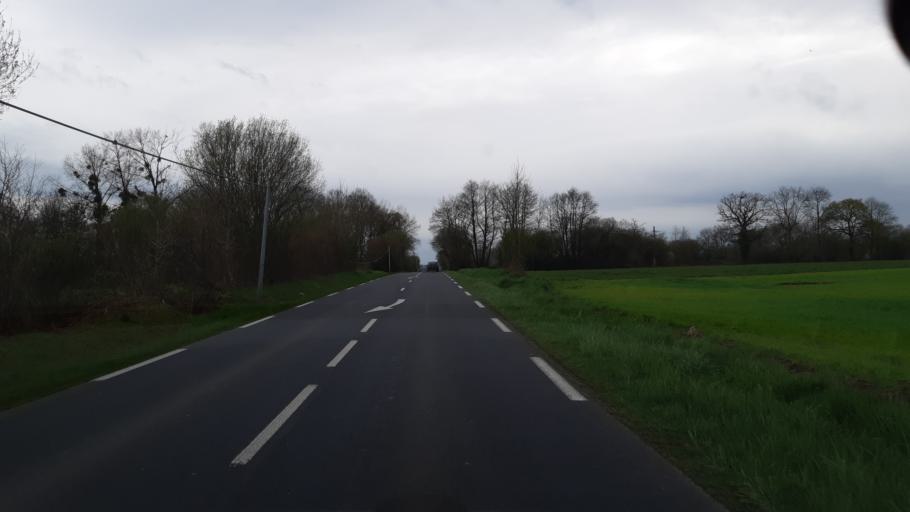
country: FR
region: Lower Normandy
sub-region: Departement de la Manche
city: Tessy-sur-Vire
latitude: 49.0181
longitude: -1.1478
